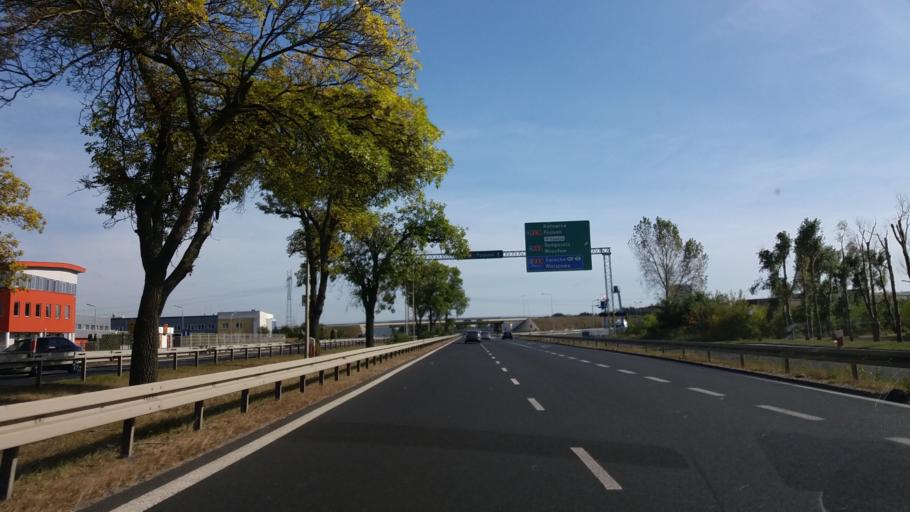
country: PL
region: Greater Poland Voivodeship
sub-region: Powiat poznanski
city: Baranowo
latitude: 52.4444
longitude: 16.7360
